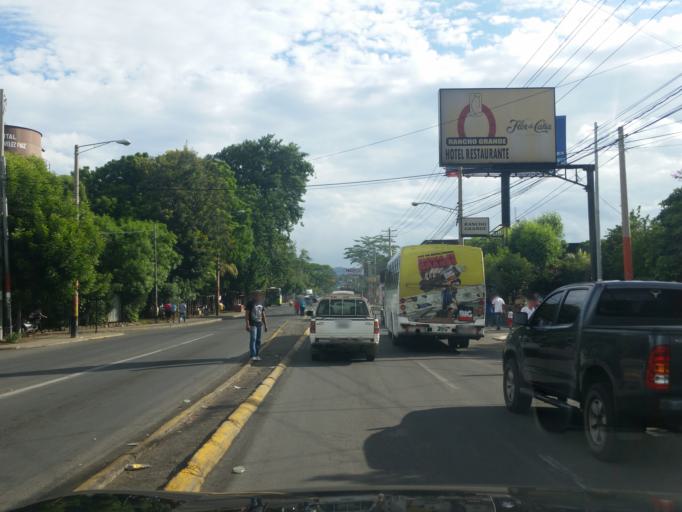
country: NI
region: Managua
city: Ciudad Sandino
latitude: 12.1292
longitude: -86.3112
